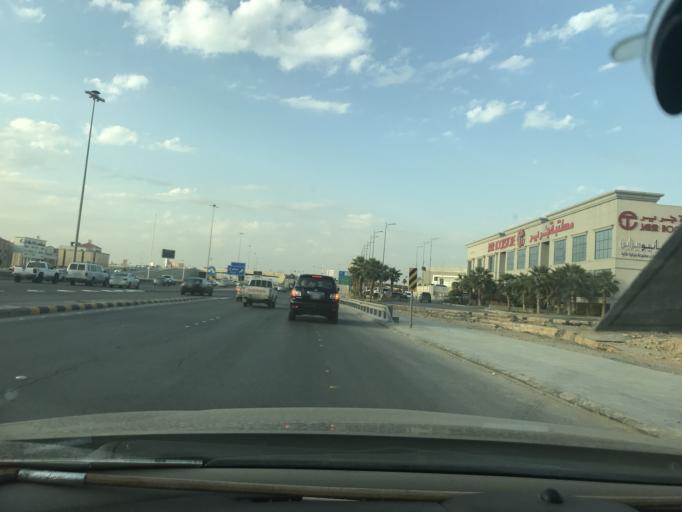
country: SA
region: Ar Riyad
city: Riyadh
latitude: 24.7507
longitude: 46.5839
